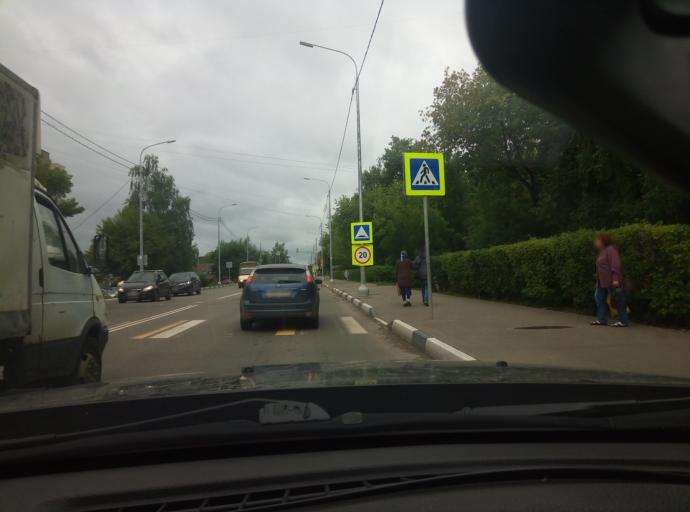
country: RU
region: Moskovskaya
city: Serpukhov
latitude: 54.9145
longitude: 37.4419
